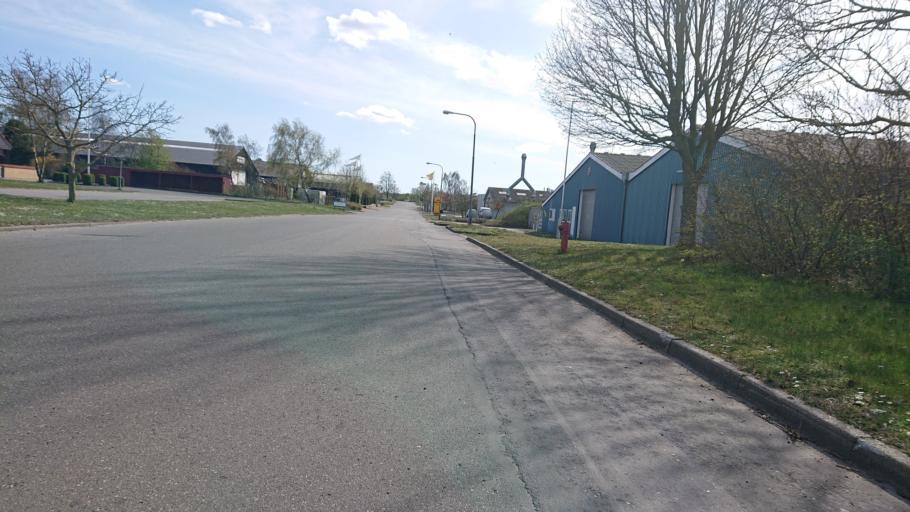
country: DK
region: South Denmark
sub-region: Nyborg Kommune
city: Nyborg
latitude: 55.3137
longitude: 10.7526
